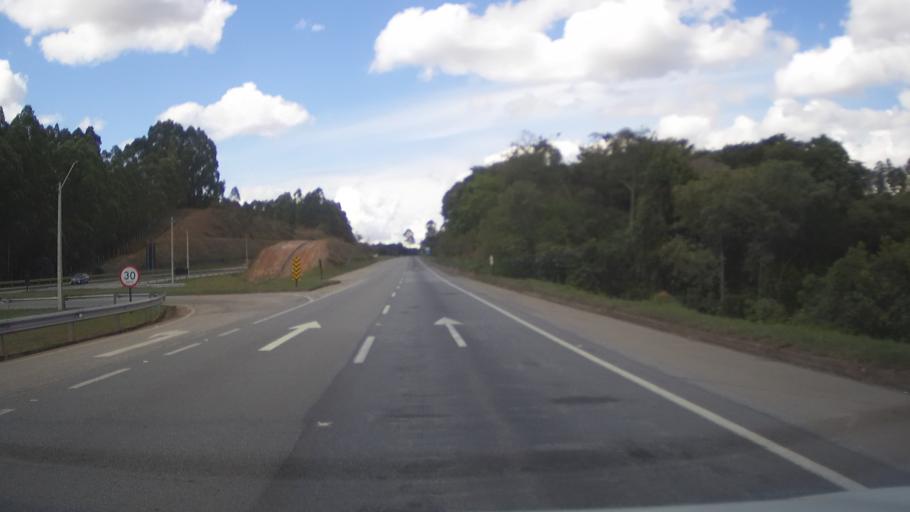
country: BR
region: Minas Gerais
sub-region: Santo Antonio Do Amparo
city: Santo Antonio do Amparo
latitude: -20.8531
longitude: -44.8360
